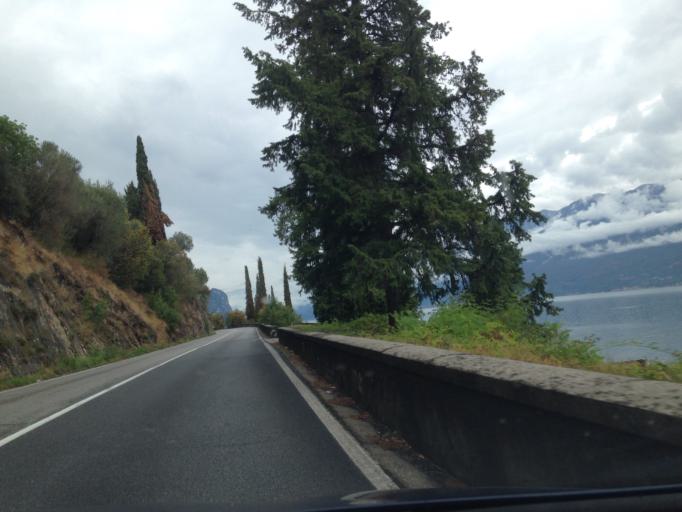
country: IT
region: Lombardy
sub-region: Provincia di Brescia
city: Gargnano
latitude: 45.6669
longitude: 10.6480
